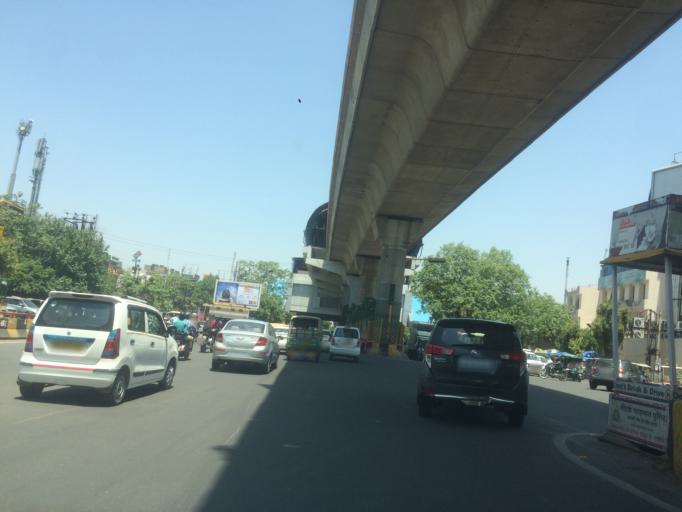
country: IN
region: Uttar Pradesh
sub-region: Gautam Buddha Nagar
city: Noida
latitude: 28.5772
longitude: 77.3188
